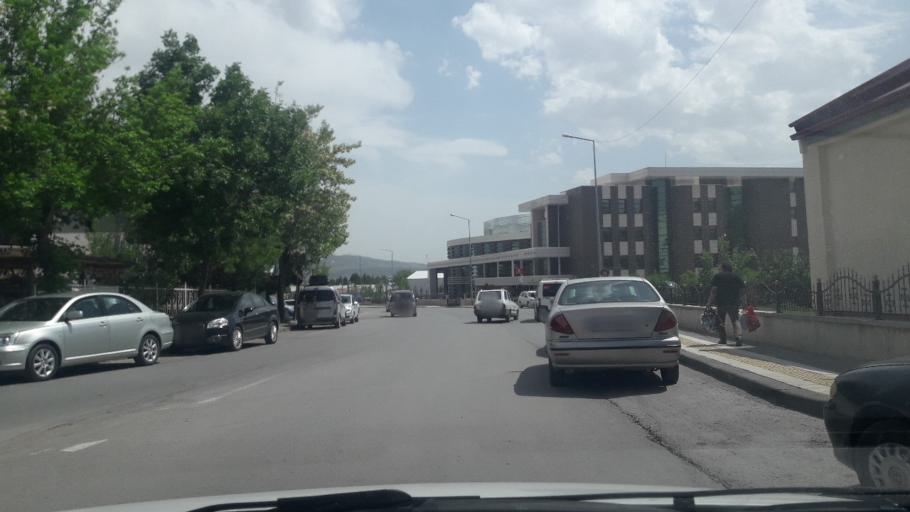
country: TR
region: Sivas
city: Sivas
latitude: 39.7434
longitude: 37.0118
